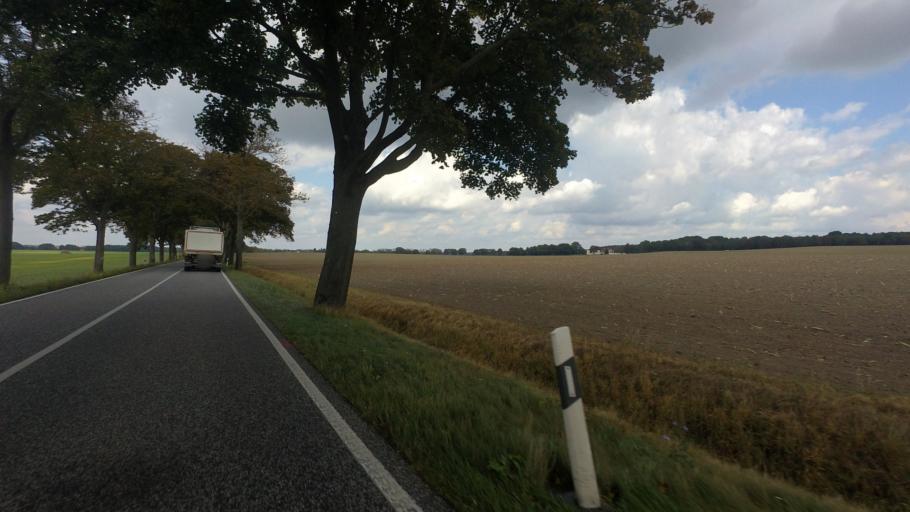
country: DE
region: Brandenburg
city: Juterbog
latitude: 51.9672
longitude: 13.1080
